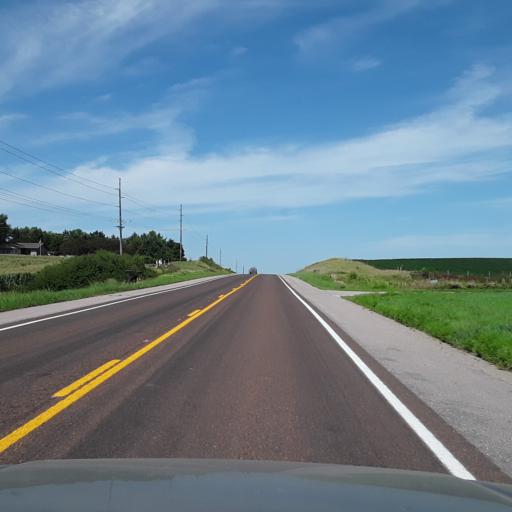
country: US
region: Nebraska
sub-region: Seward County
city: Milford
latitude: 40.8865
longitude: -96.8864
